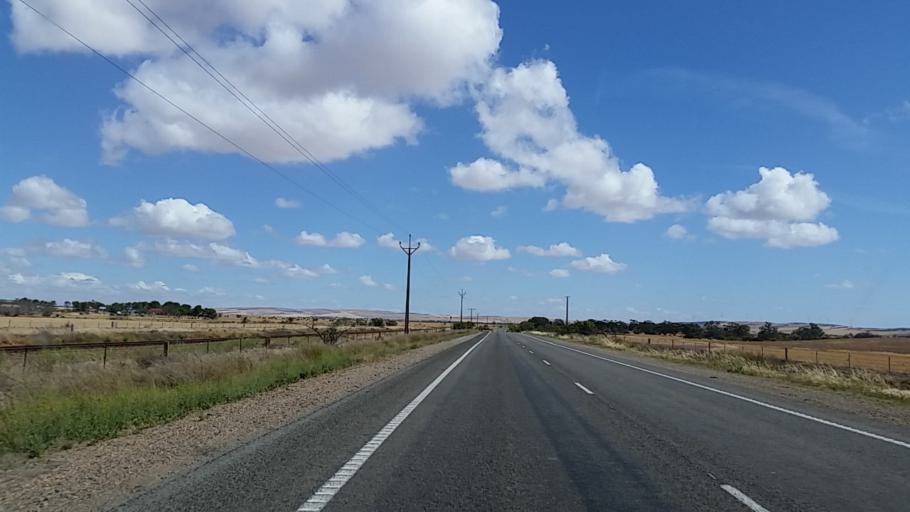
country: AU
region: South Australia
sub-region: Port Pirie City and Dists
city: Crystal Brook
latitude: -33.3980
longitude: 138.1684
